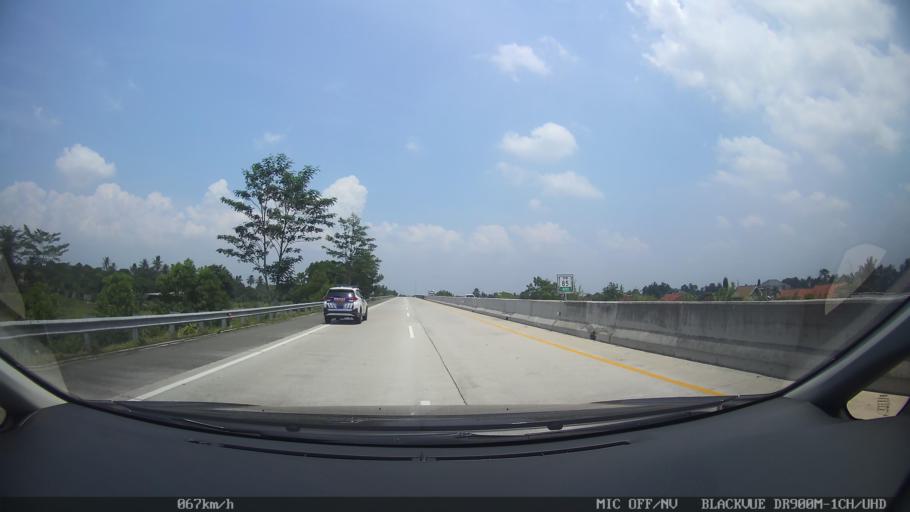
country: ID
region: Lampung
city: Kedaton
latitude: -5.3280
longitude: 105.2851
